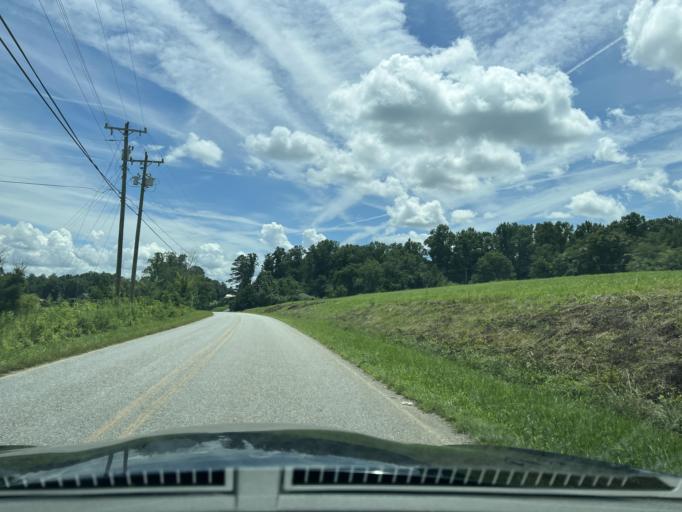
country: US
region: North Carolina
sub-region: Henderson County
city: Fruitland
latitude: 35.4037
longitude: -82.3910
